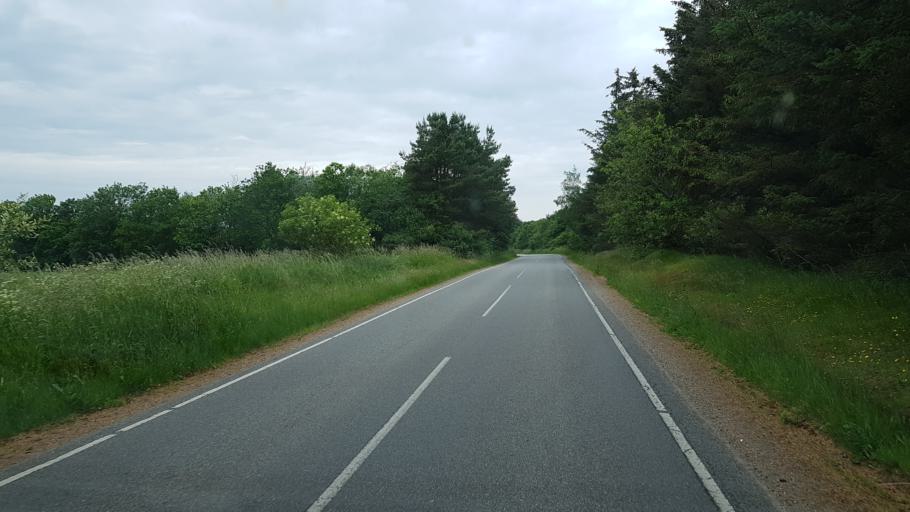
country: DK
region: South Denmark
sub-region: Varde Kommune
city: Oksbol
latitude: 55.6652
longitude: 8.3066
